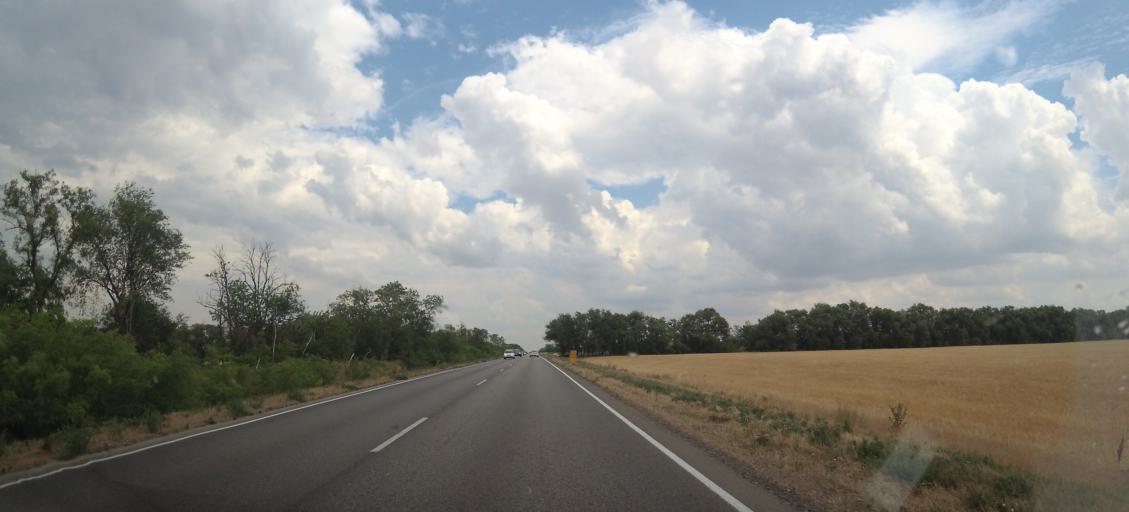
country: RU
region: Rostov
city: Peschanokopskoye
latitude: 46.0866
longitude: 41.0867
